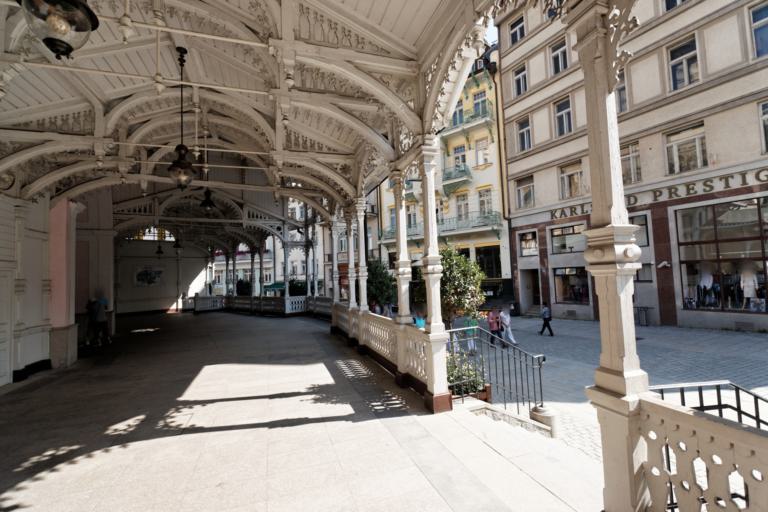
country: CZ
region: Karlovarsky
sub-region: Okres Karlovy Vary
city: Karlovy Vary
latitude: 50.2235
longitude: 12.8834
